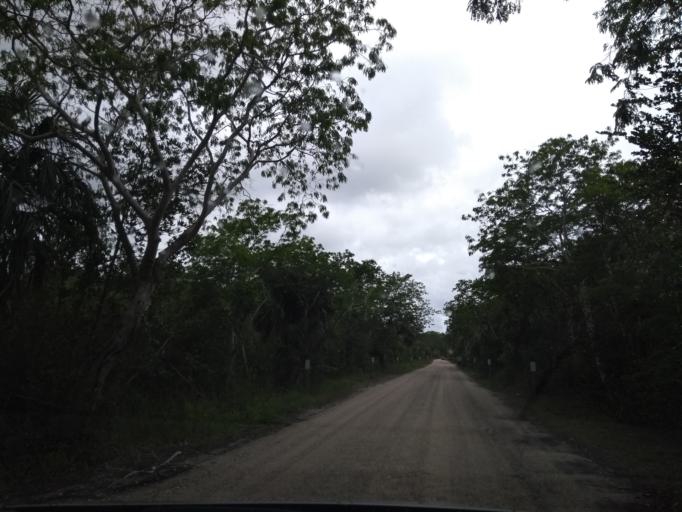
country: US
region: Florida
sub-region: Miami-Dade County
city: The Hammocks
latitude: 25.7465
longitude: -80.9505
